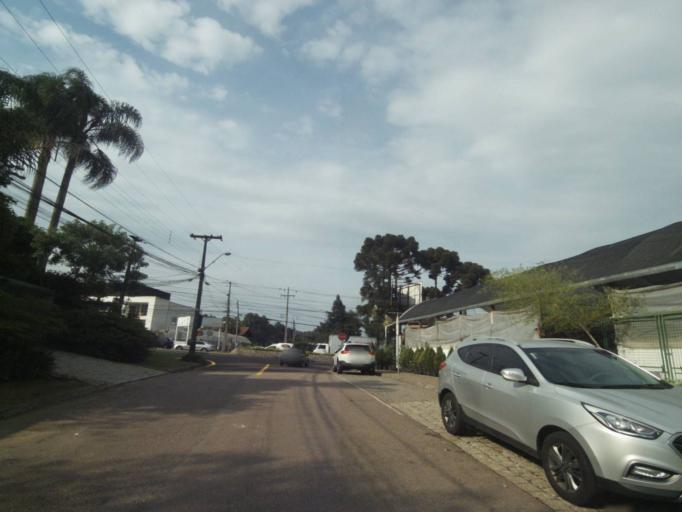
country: BR
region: Parana
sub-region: Curitiba
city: Curitiba
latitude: -25.4145
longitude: -49.3102
